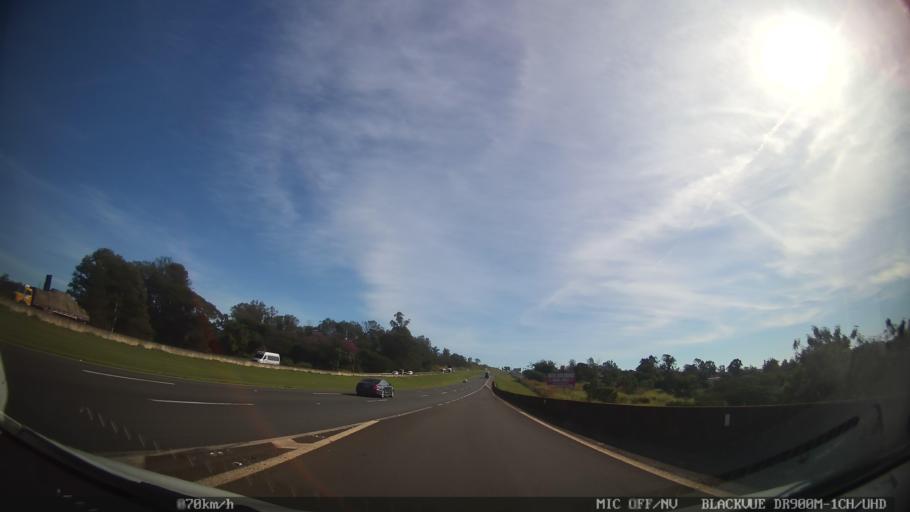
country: BR
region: Sao Paulo
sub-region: Araras
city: Araras
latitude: -22.3940
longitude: -47.3916
